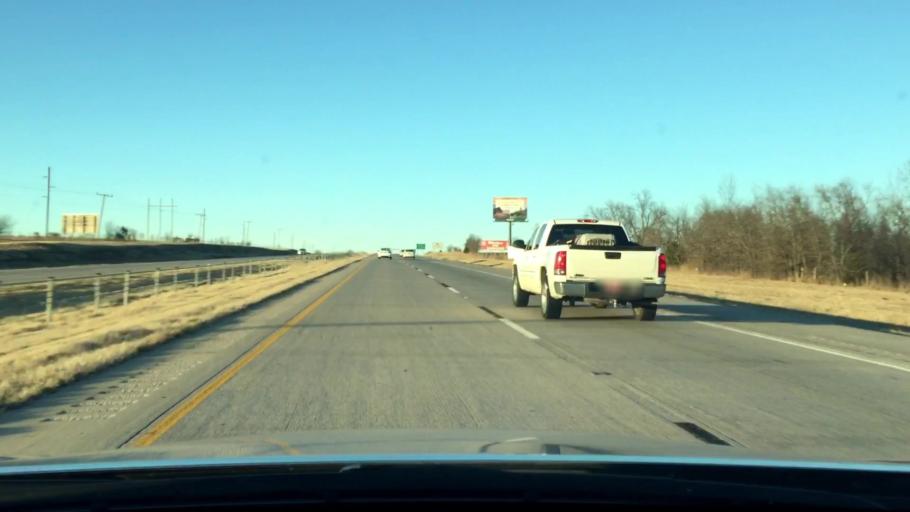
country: US
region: Oklahoma
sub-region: Love County
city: Marietta
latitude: 33.8864
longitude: -97.1343
